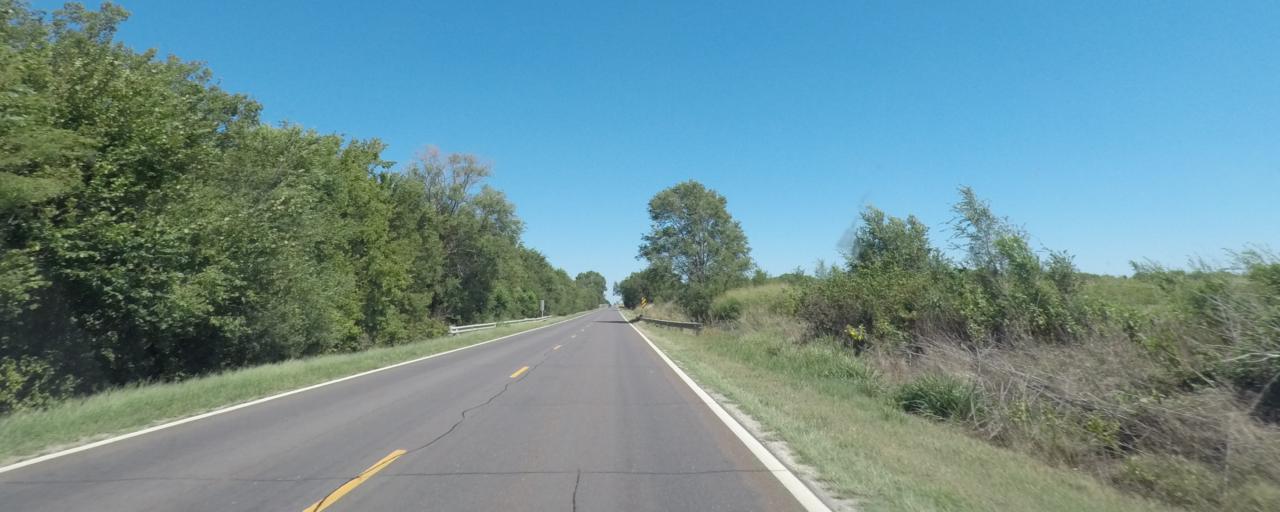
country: US
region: Kansas
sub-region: Sumner County
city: Wellington
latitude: 37.0758
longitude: -97.4014
